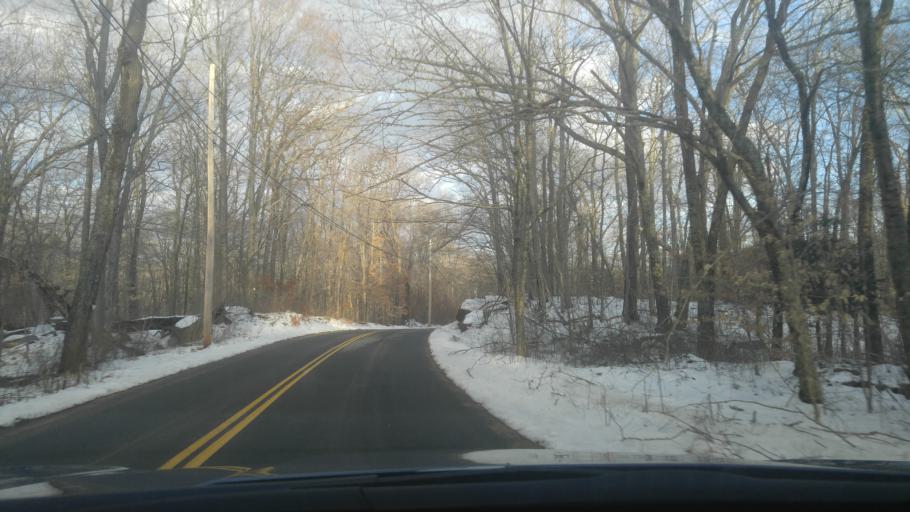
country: US
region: Rhode Island
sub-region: Kent County
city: Coventry
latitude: 41.7205
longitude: -71.6883
